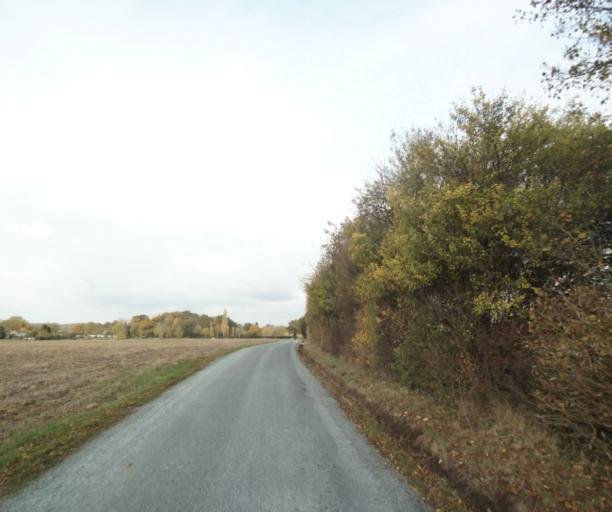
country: FR
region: Poitou-Charentes
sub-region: Departement de la Charente-Maritime
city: Saint-Georges-des-Coteaux
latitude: 45.7718
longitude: -0.6958
